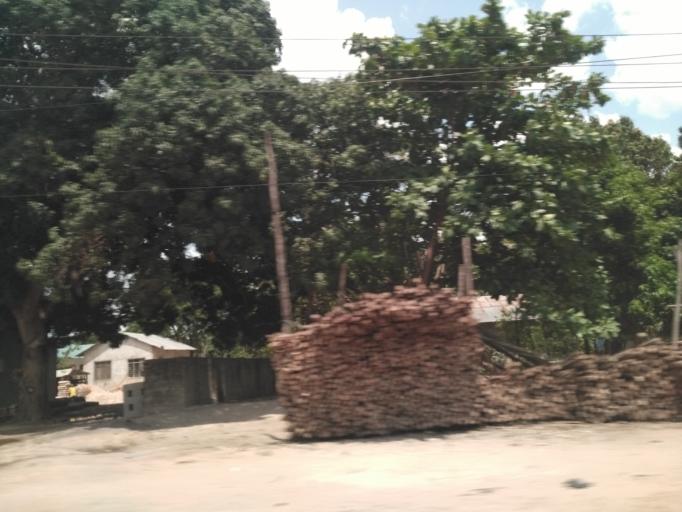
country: TZ
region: Dar es Salaam
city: Dar es Salaam
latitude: -6.8835
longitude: 39.3414
